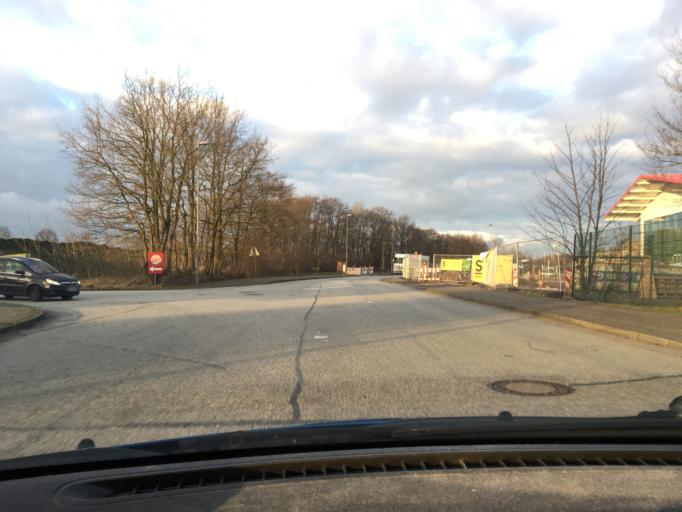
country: DE
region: Schleswig-Holstein
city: Kolln-Reisiek
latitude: 53.7455
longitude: 9.7064
